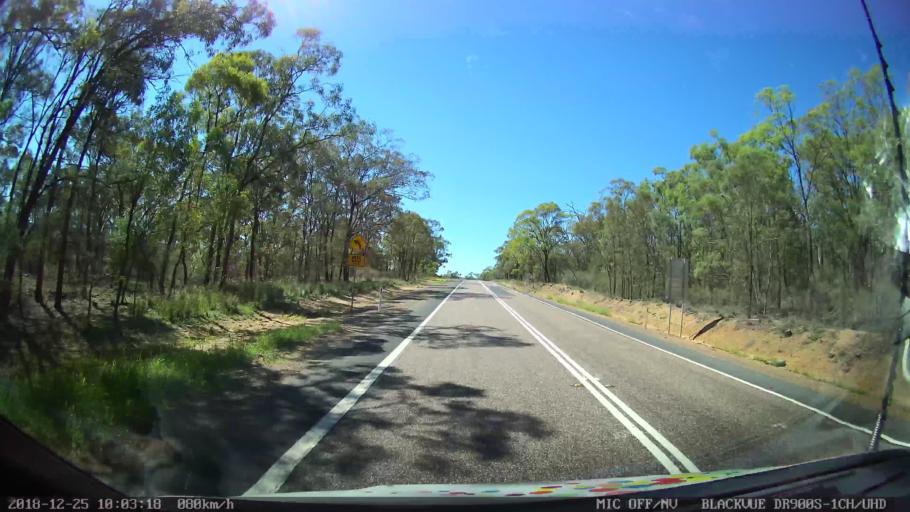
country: AU
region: New South Wales
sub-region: Upper Hunter Shire
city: Merriwa
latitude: -32.2271
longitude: 150.4699
